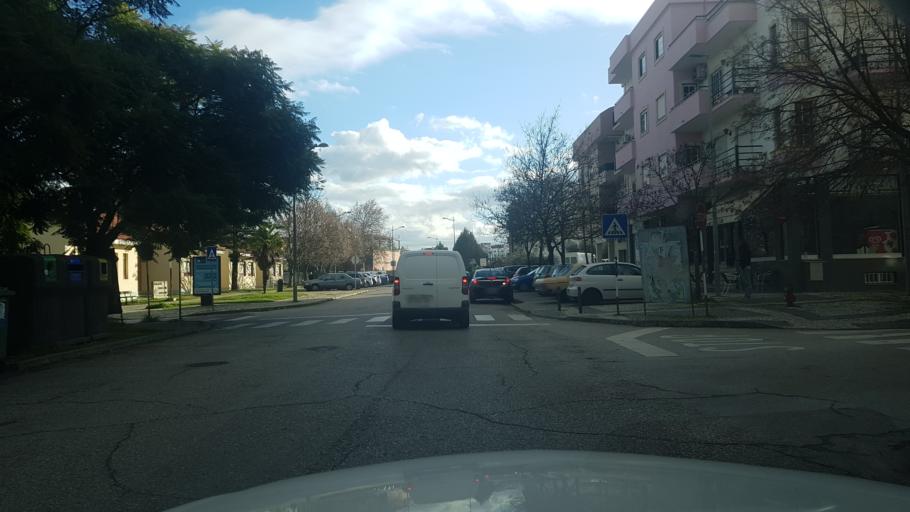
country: PT
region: Santarem
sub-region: Entroncamento
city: Entroncamento
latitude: 39.4666
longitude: -8.4720
